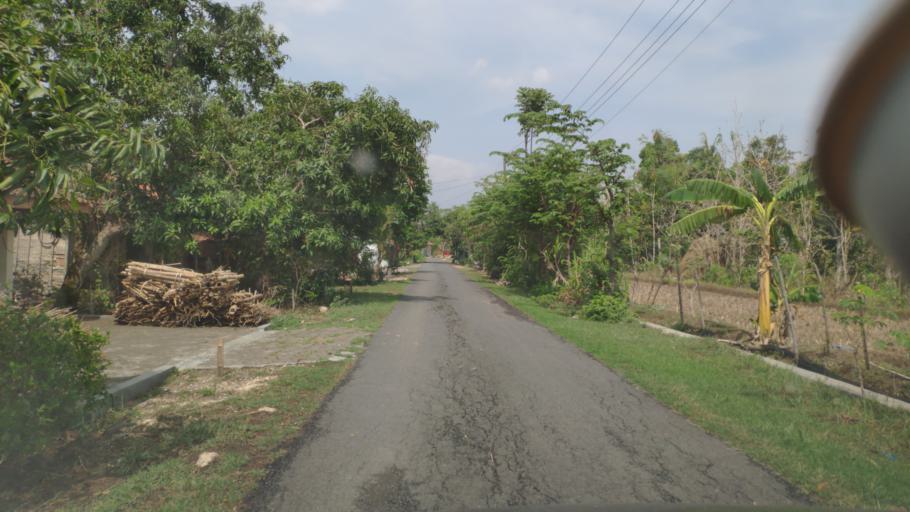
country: ID
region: Central Java
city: Balongrejo
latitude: -7.0050
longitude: 111.3750
